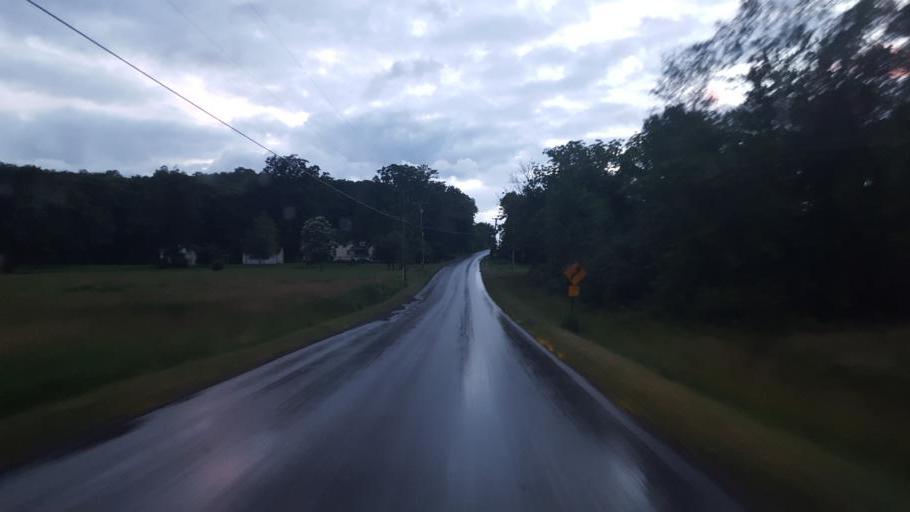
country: US
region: New York
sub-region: Wayne County
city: Clyde
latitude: 43.0451
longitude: -76.8895
